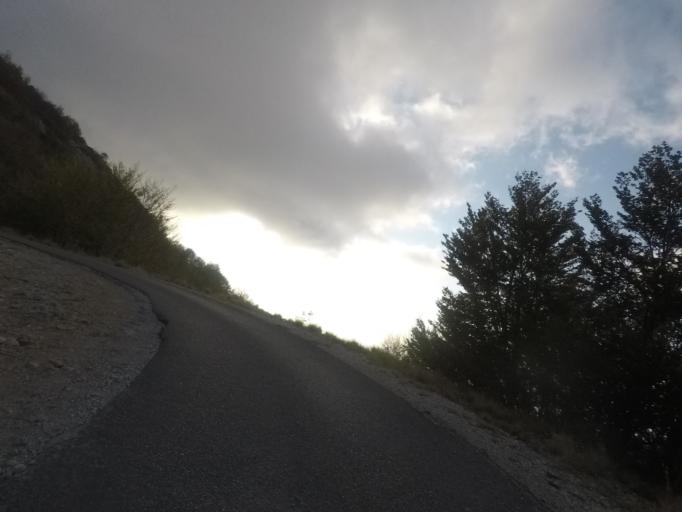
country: ME
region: Kotor
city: Kotor
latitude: 42.4175
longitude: 18.8037
